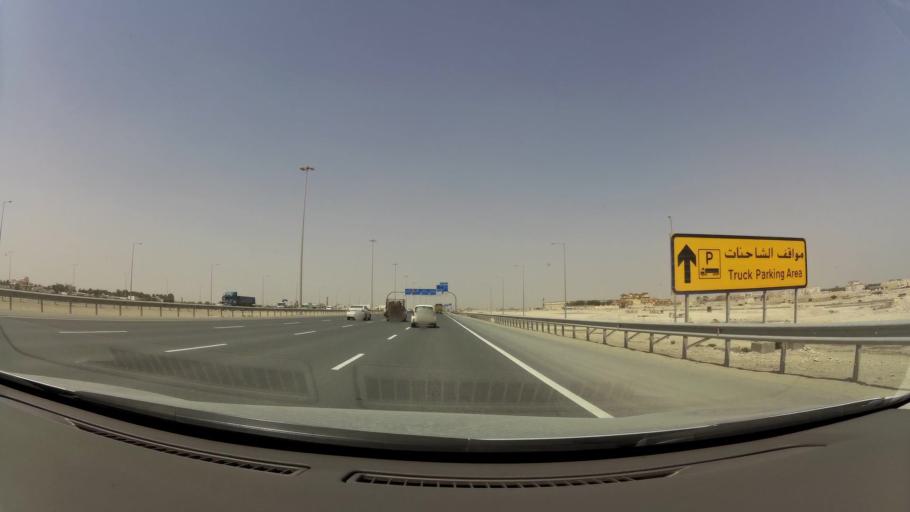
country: QA
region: Baladiyat Umm Salal
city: Umm Salal Muhammad
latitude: 25.4286
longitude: 51.4159
